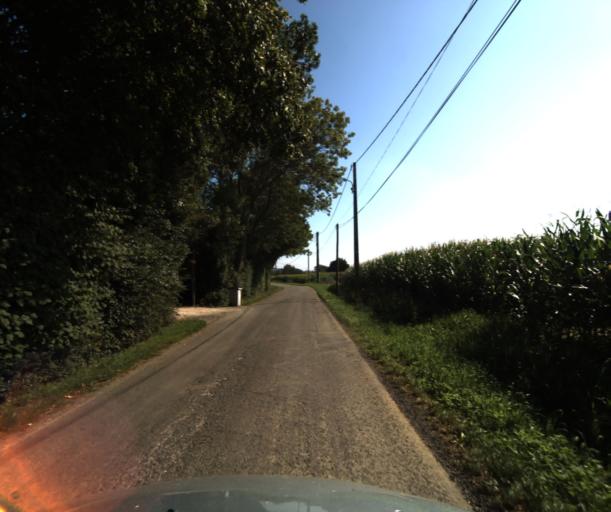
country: FR
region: Midi-Pyrenees
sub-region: Departement de la Haute-Garonne
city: Le Fauga
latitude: 43.4126
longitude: 1.3050
